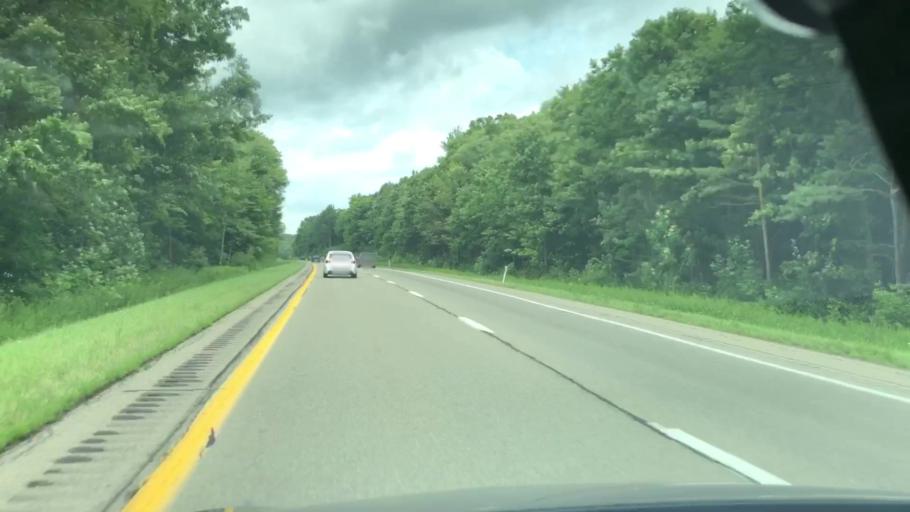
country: US
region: Pennsylvania
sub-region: Erie County
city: Edinboro
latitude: 41.7960
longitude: -80.1751
